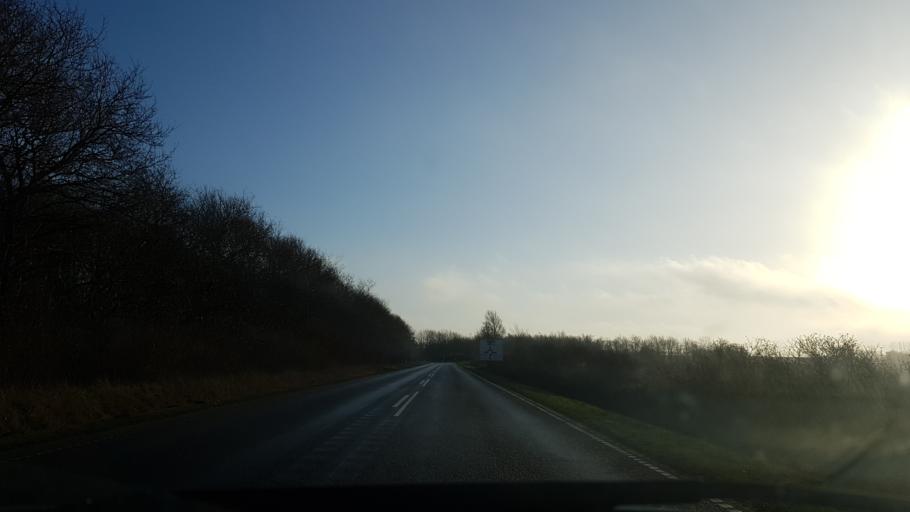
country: DK
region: South Denmark
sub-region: Haderslev Kommune
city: Vojens
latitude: 55.2011
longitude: 9.1950
